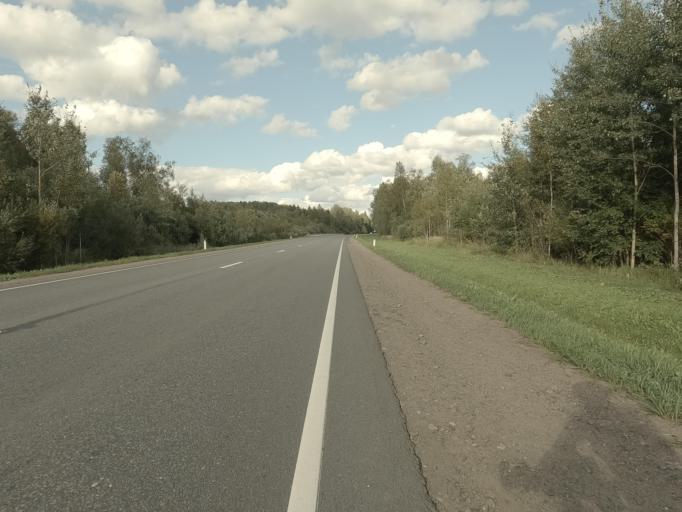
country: RU
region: Leningrad
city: Nikol'skoye
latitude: 59.6646
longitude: 30.8805
